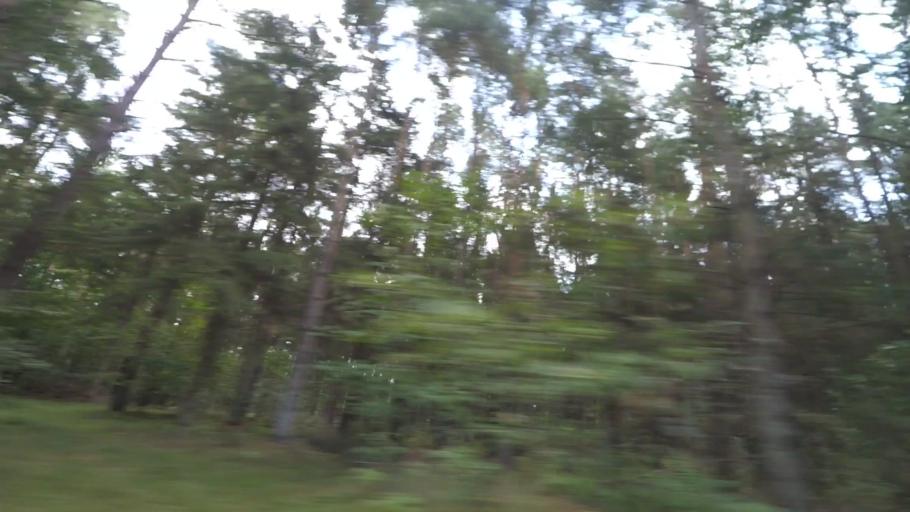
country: DK
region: Central Jutland
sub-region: Syddjurs Kommune
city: Ryomgard
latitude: 56.4793
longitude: 10.4873
